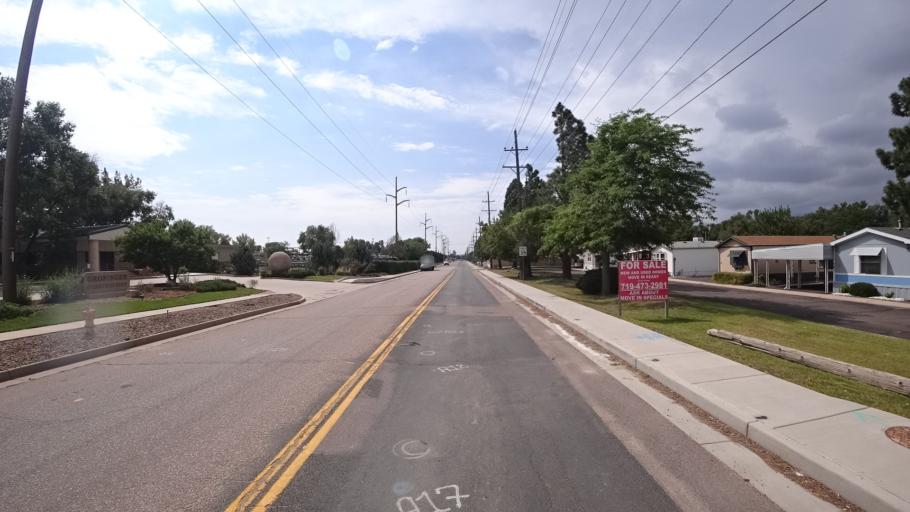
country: US
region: Colorado
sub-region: El Paso County
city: Colorado Springs
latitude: 38.8851
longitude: -104.8225
